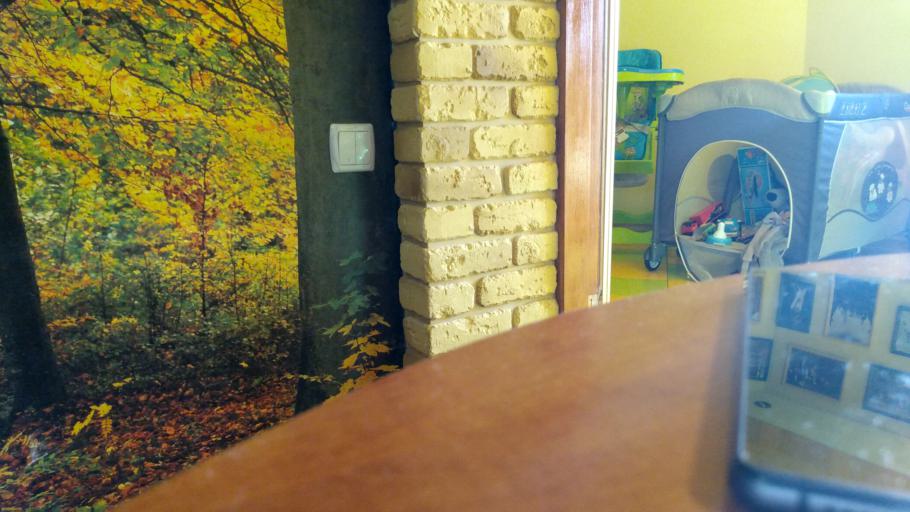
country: RU
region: Tverskaya
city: Likhoslavl'
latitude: 57.1427
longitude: 35.6220
